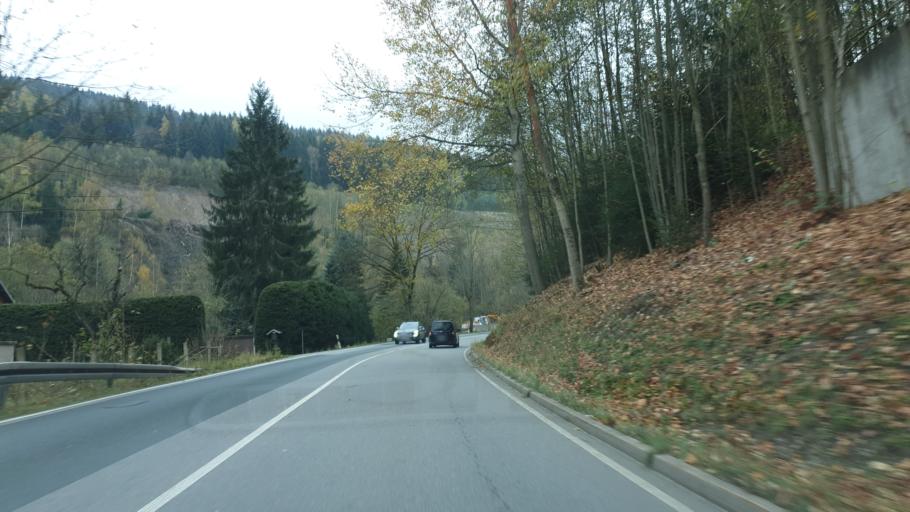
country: DE
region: Saxony
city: Breitenbrunn
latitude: 50.5065
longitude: 12.7730
